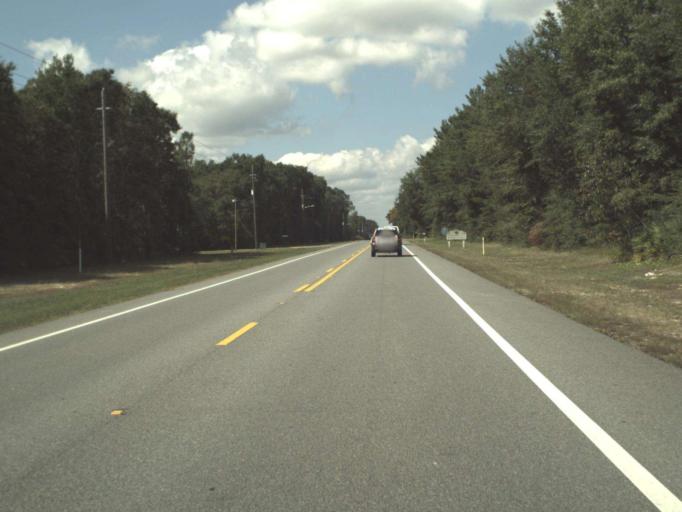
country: US
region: Florida
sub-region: Walton County
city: Freeport
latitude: 30.4855
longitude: -86.1091
